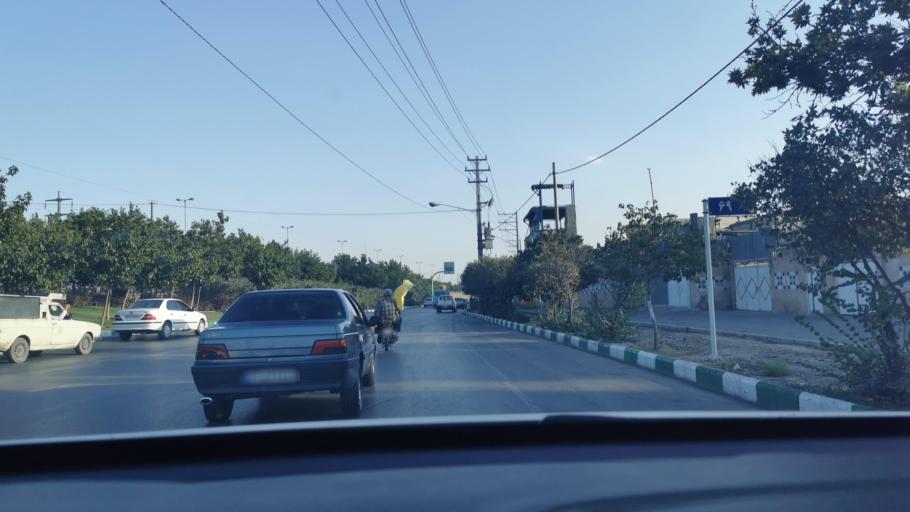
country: IR
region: Razavi Khorasan
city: Mashhad
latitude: 36.2869
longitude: 59.6580
